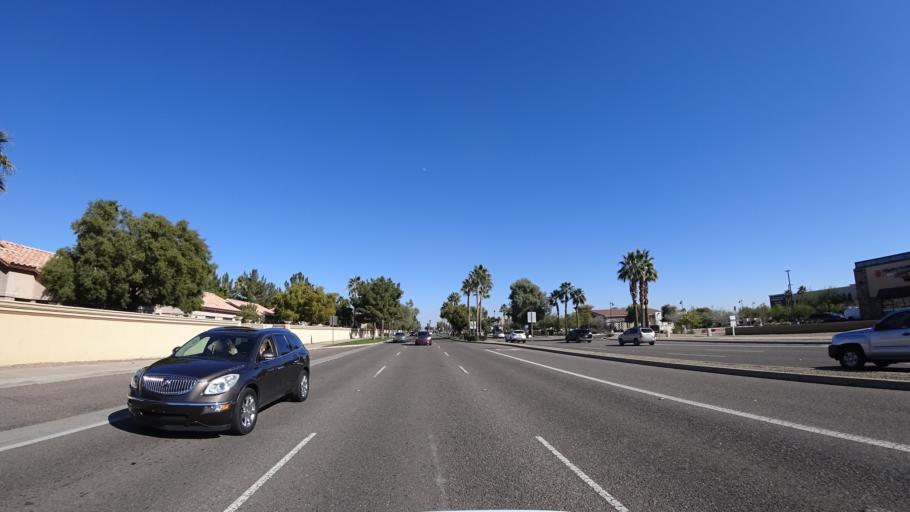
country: US
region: Arizona
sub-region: Maricopa County
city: Sun City West
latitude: 33.6387
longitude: -112.3675
